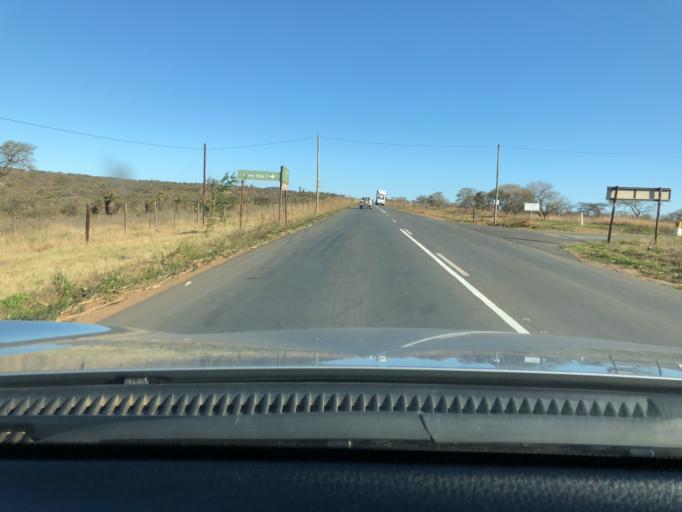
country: ZA
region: KwaZulu-Natal
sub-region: uMgungundlovu District Municipality
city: Camperdown
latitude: -29.8190
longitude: 30.5227
